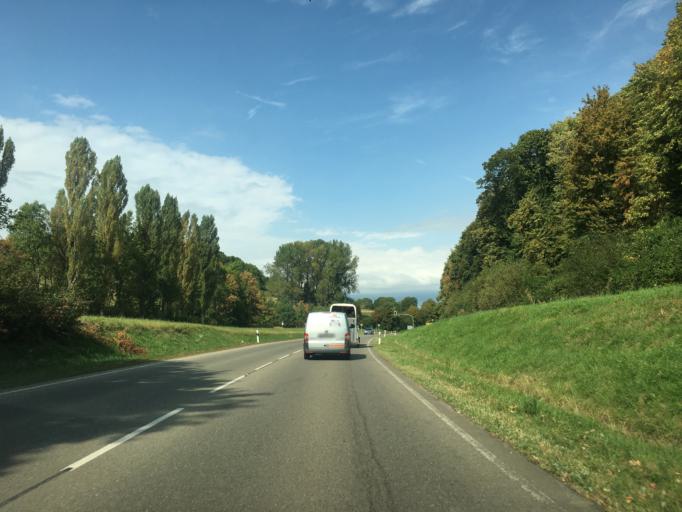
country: DE
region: Baden-Wuerttemberg
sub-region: Tuebingen Region
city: Gomaringen
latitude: 48.4543
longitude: 9.1510
